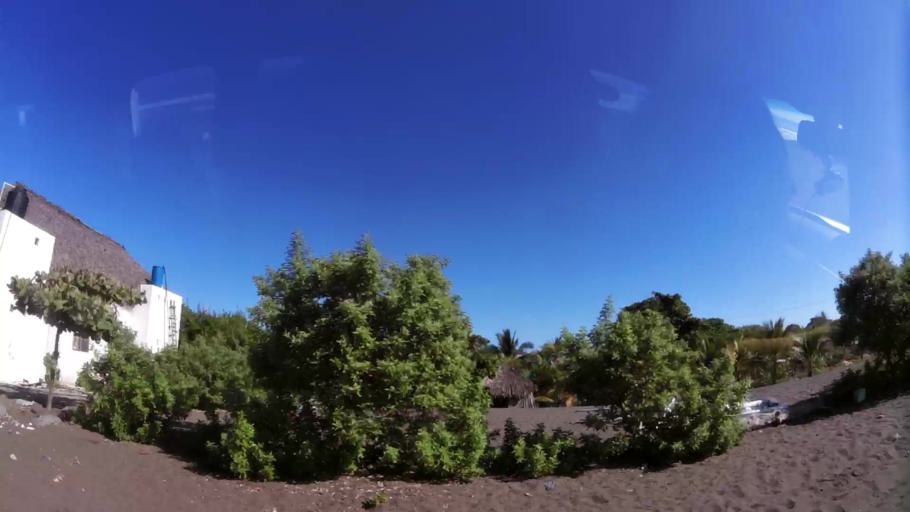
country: GT
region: Jutiapa
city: Pasaco
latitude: 13.8470
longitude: -90.3684
